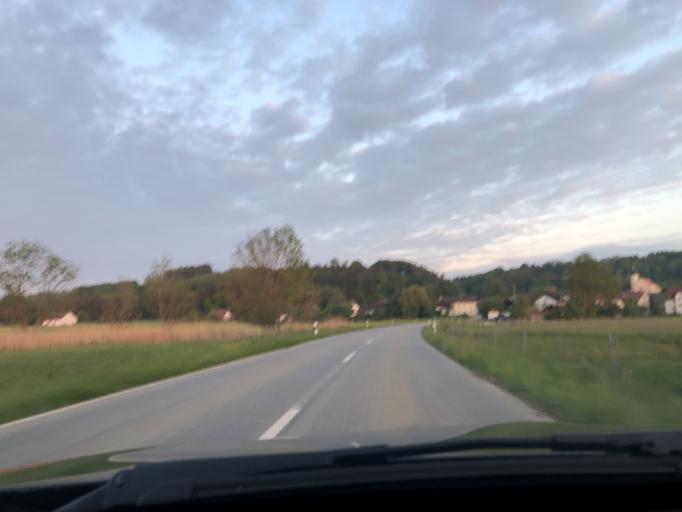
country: DE
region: Bavaria
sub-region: Upper Bavaria
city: Wolfersdorf
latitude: 48.4436
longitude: 11.7213
